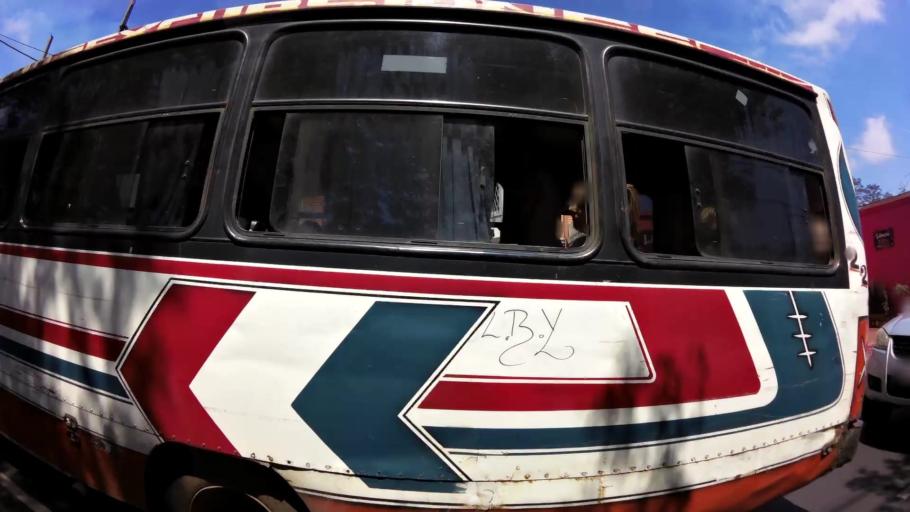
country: PY
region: Central
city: San Lorenzo
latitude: -25.3402
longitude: -57.5088
